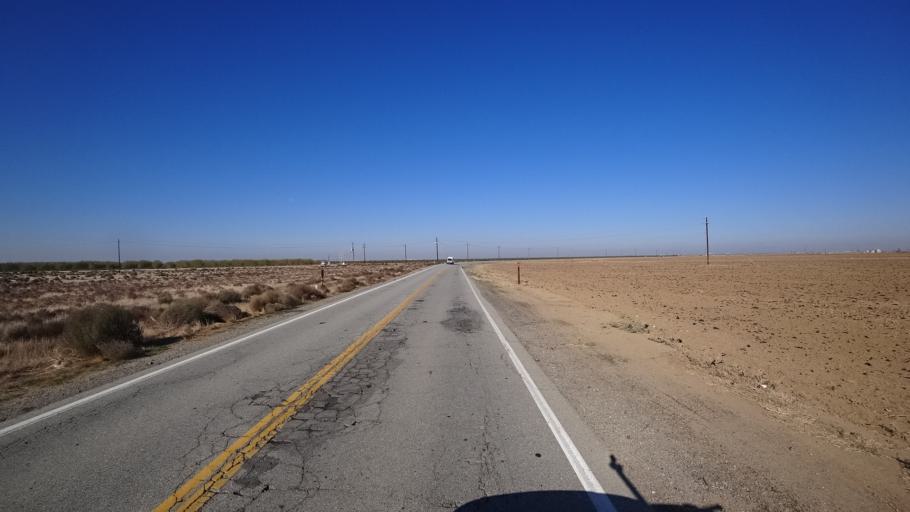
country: US
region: California
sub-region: Kern County
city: Rosedale
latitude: 35.4332
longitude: -119.1522
